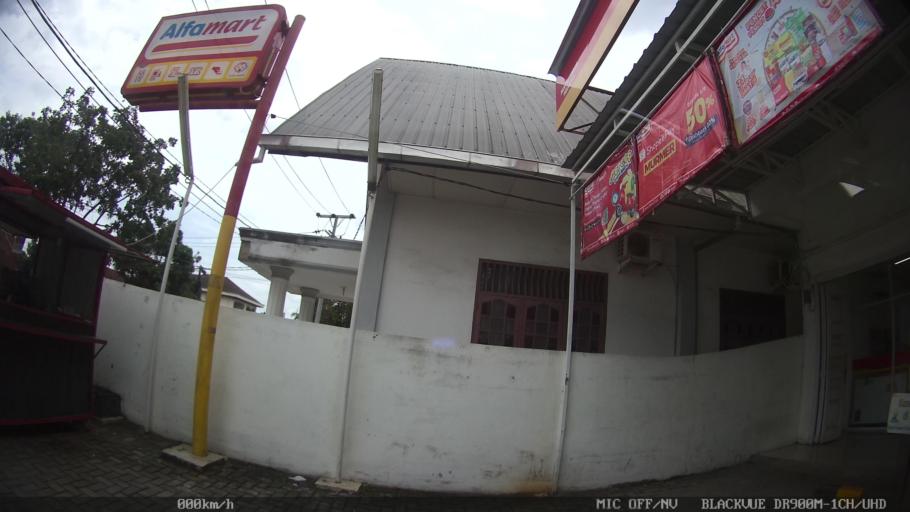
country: ID
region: North Sumatra
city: Sunggal
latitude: 3.5973
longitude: 98.6176
